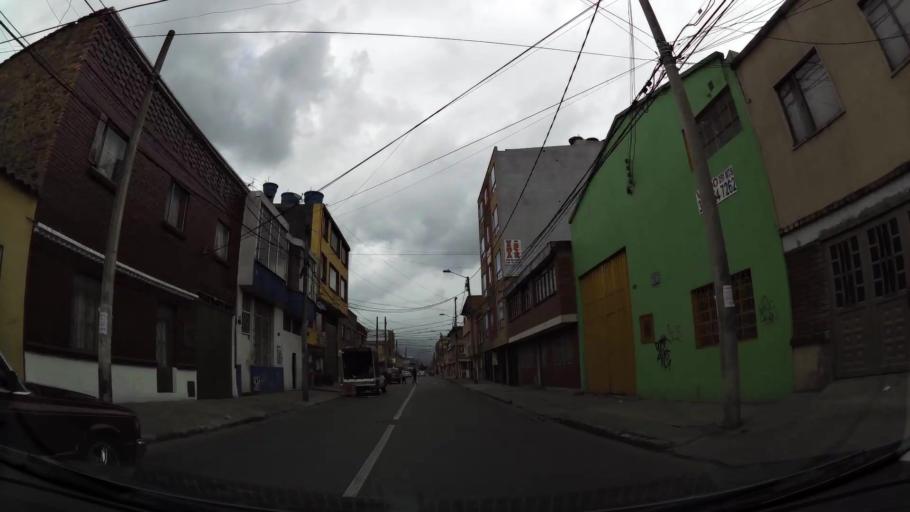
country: CO
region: Bogota D.C.
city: Barrio San Luis
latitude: 4.6983
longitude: -74.1028
